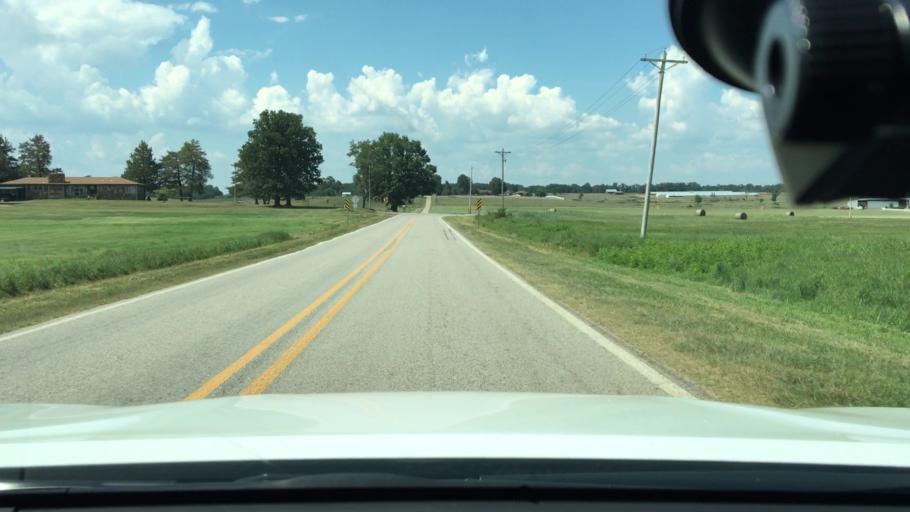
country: US
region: Arkansas
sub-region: Johnson County
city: Coal Hill
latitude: 35.3490
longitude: -93.5886
